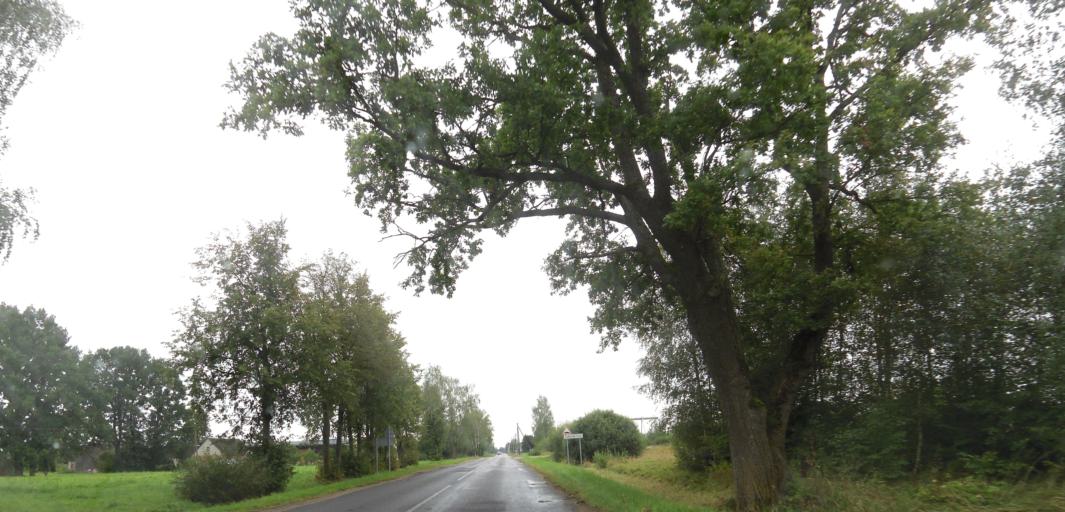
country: LT
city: Sirvintos
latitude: 55.0586
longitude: 24.9544
